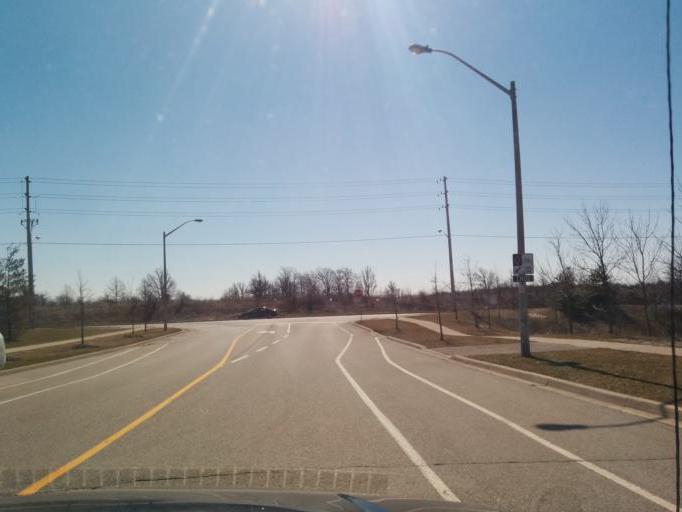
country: CA
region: Ontario
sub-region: Halton
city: Milton
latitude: 43.5054
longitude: -79.8400
